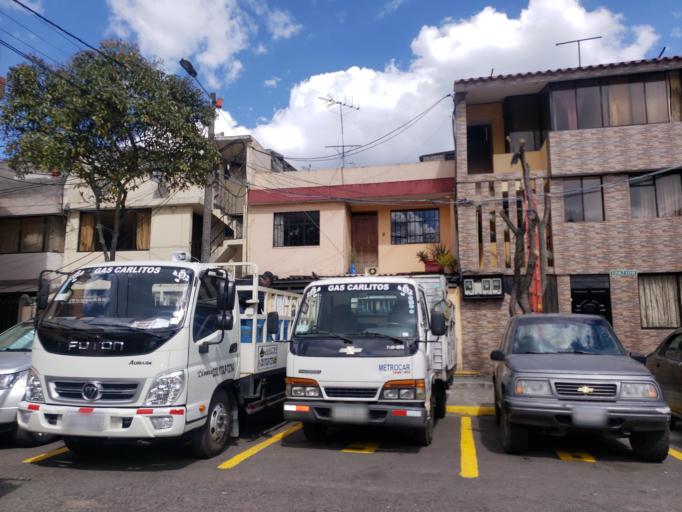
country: EC
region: Pichincha
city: Quito
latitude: -0.2712
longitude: -78.5390
